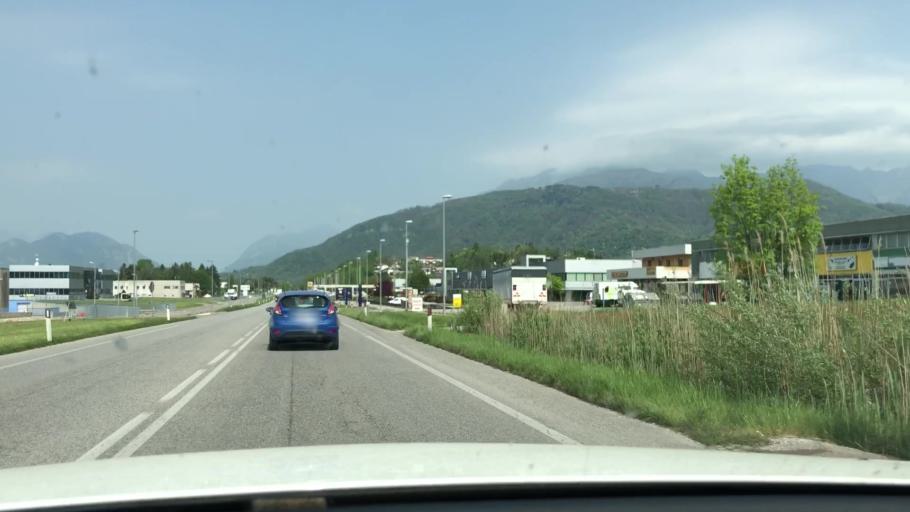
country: IT
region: Friuli Venezia Giulia
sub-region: Provincia di Udine
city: Magnano in Riviera
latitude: 46.2033
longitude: 13.1899
